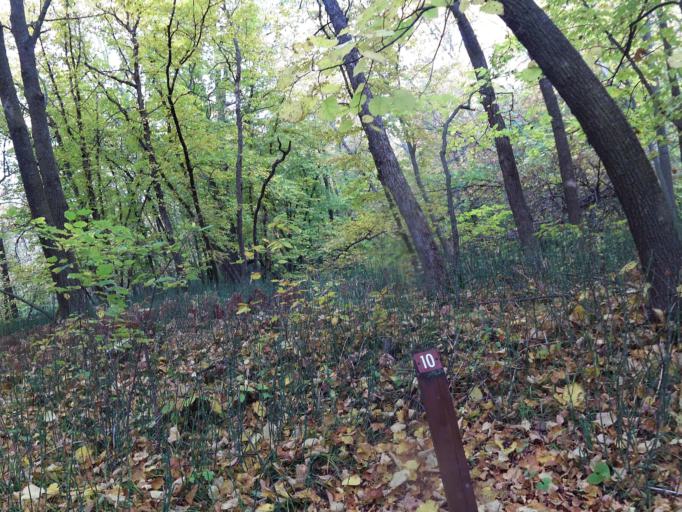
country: US
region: North Dakota
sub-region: Pembina County
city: Cavalier
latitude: 48.7760
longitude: -97.7372
